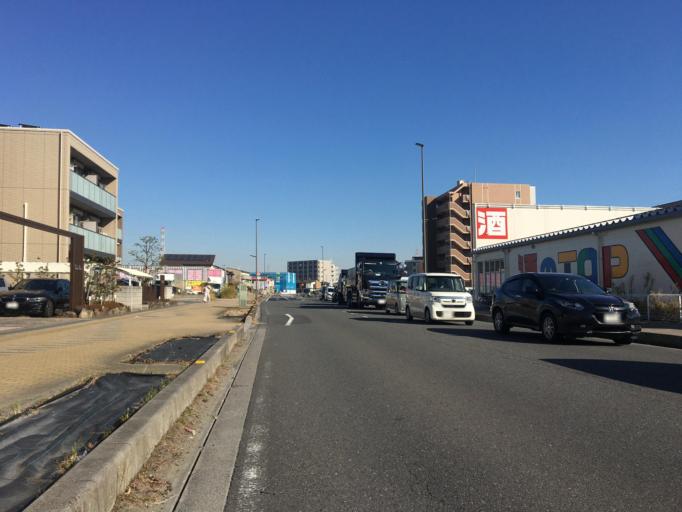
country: JP
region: Saitama
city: Yashio-shi
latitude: 35.8118
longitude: 139.8473
